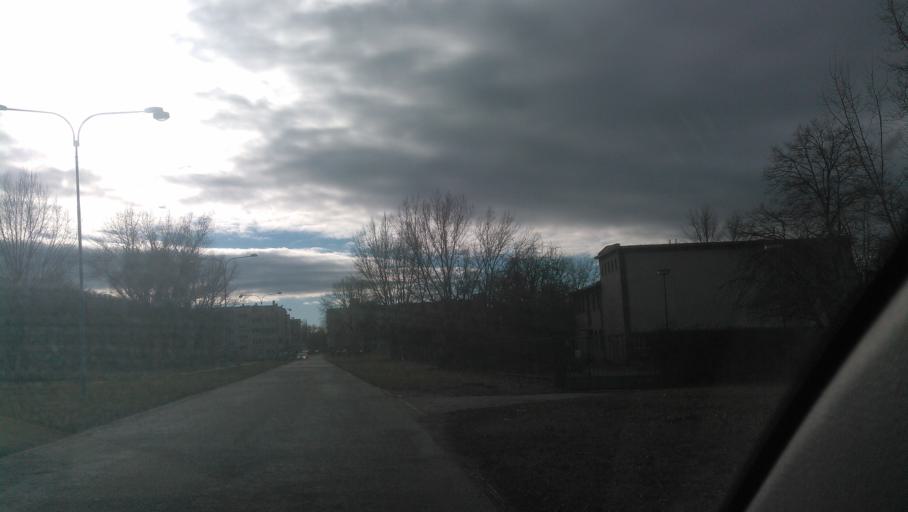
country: SK
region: Trnavsky
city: Hlohovec
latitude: 48.4224
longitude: 17.7844
